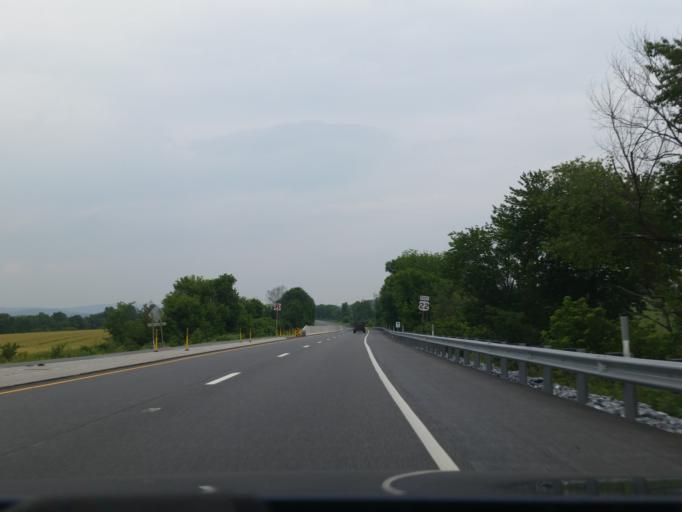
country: US
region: Pennsylvania
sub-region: Lebanon County
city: Jonestown
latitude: 40.4286
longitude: -76.4547
